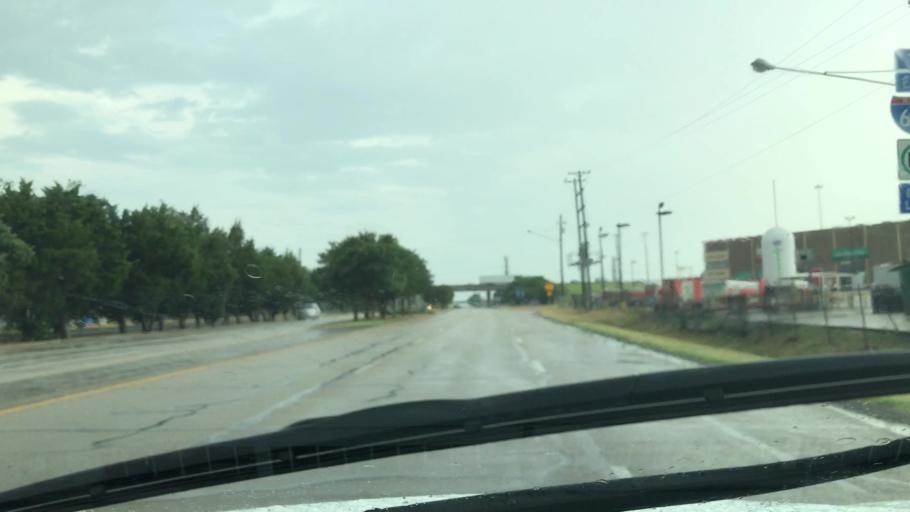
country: US
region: Texas
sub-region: Dallas County
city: Garland
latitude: 32.8710
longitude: -96.6660
